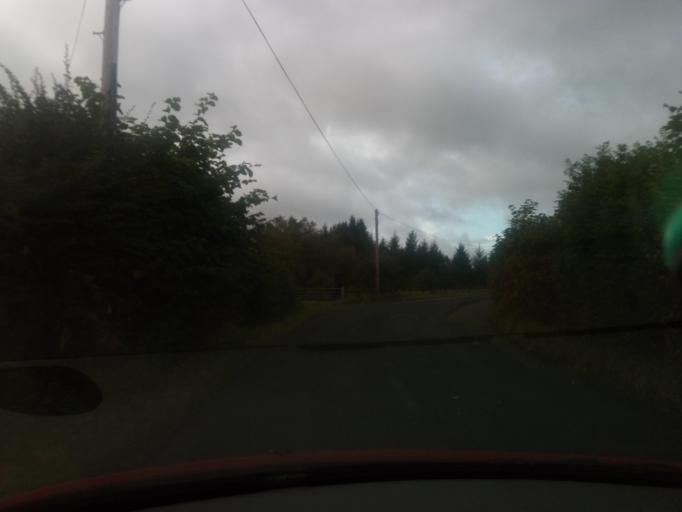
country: GB
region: Scotland
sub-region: The Scottish Borders
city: Jedburgh
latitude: 55.4538
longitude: -2.5598
